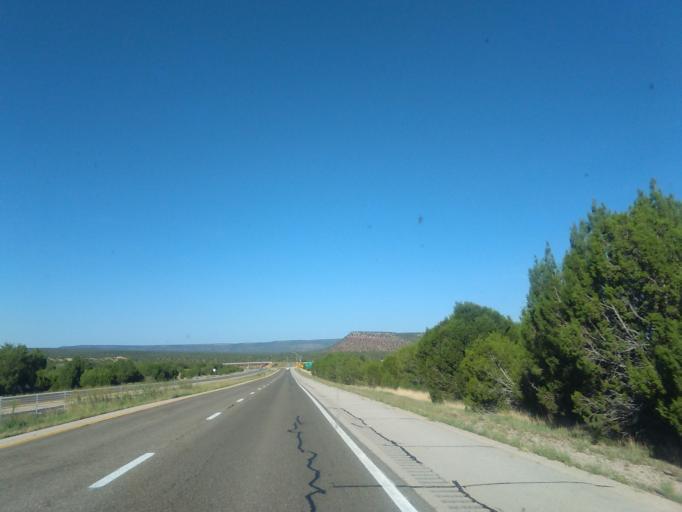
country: US
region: New Mexico
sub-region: San Miguel County
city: Las Vegas
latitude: 35.3935
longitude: -105.3326
